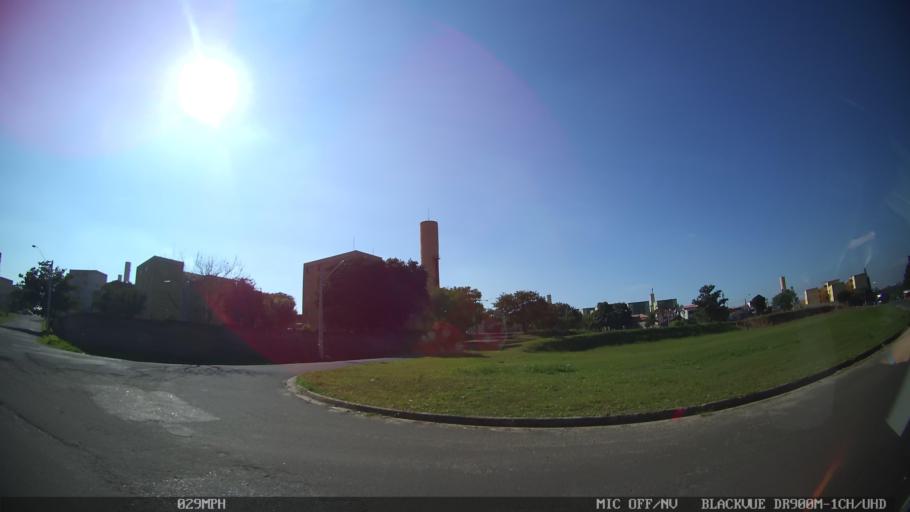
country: BR
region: Sao Paulo
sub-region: Campinas
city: Campinas
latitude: -22.9490
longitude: -47.1243
